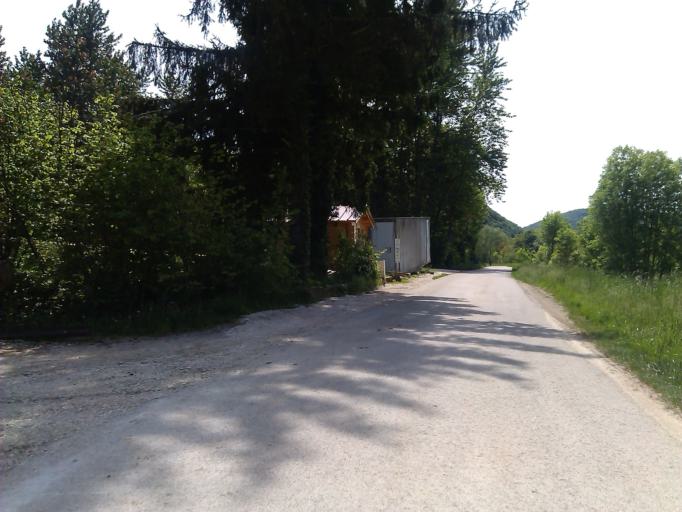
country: FR
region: Franche-Comte
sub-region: Departement du Doubs
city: Avanne-Aveney
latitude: 47.1795
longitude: 5.9458
